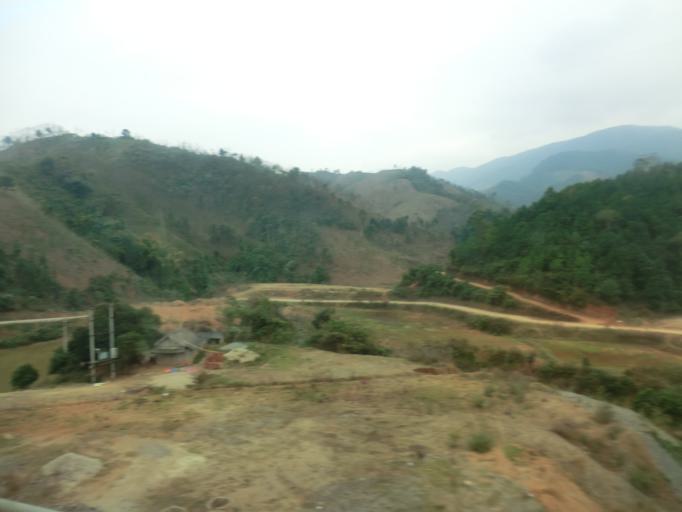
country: VN
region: Lao Cai
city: Thi Tran Pho Lu
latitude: 22.2264
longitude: 104.2820
